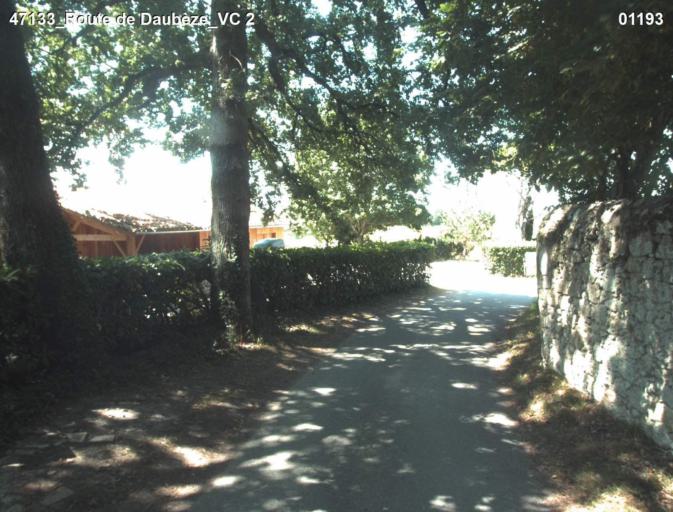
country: FR
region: Aquitaine
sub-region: Departement du Lot-et-Garonne
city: Laplume
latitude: 44.0811
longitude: 0.5471
